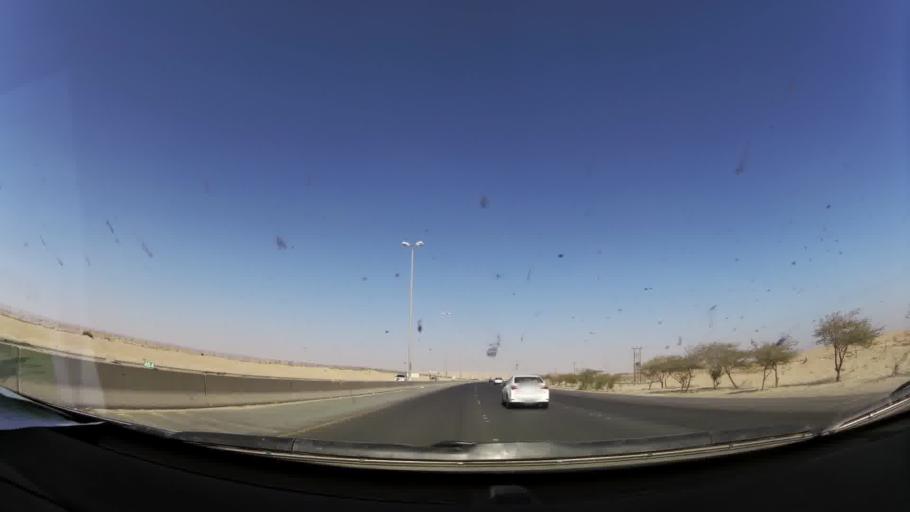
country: KW
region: Muhafazat al Jahra'
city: Al Jahra'
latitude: 29.3544
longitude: 47.6331
